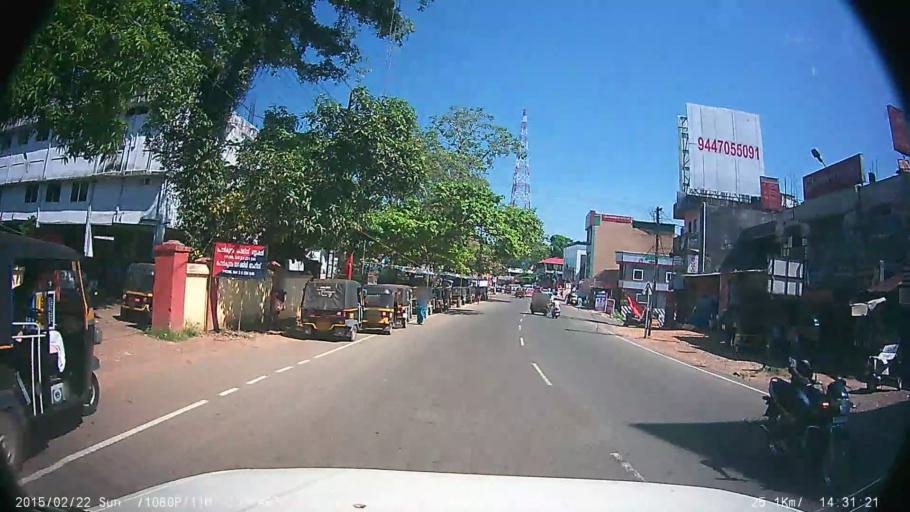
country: IN
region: Kerala
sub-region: Kottayam
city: Erattupetta
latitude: 9.5656
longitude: 76.7546
